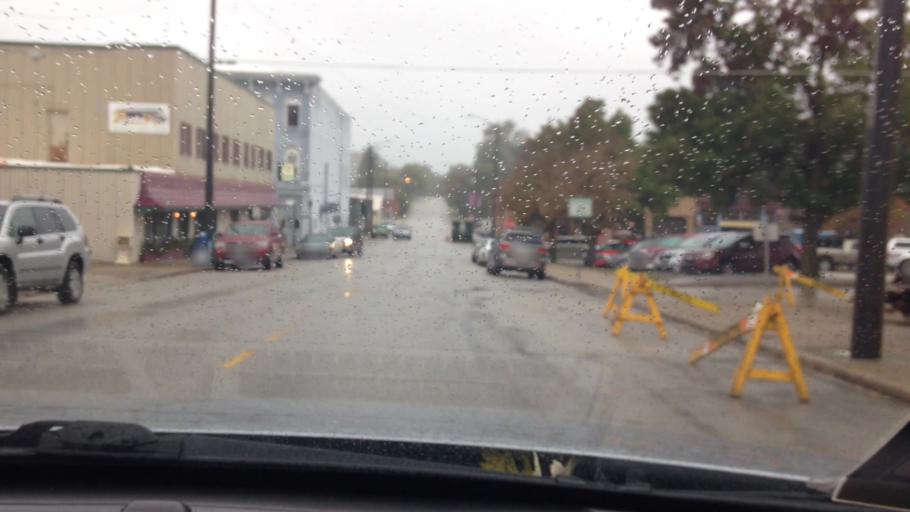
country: US
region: Kansas
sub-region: Leavenworth County
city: Leavenworth
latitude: 39.3181
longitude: -94.9122
